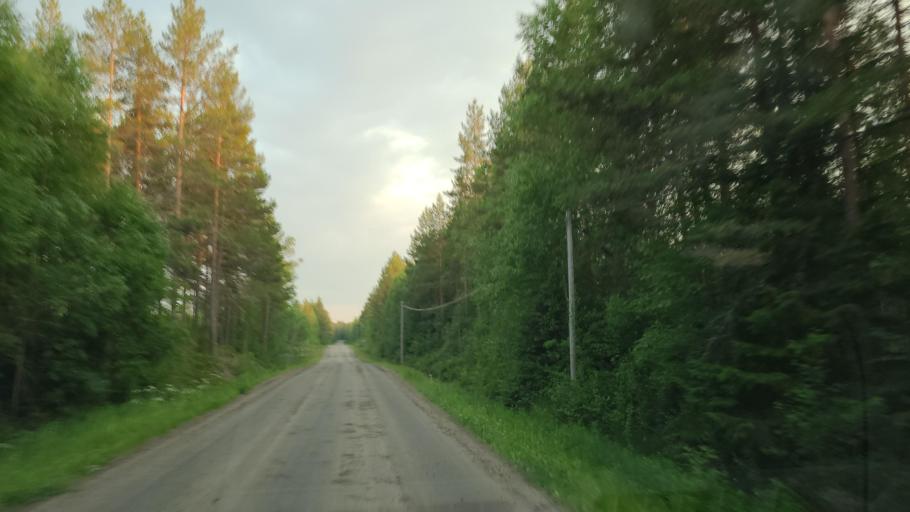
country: SE
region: Vaesterbotten
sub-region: Robertsfors Kommun
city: Robertsfors
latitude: 64.0765
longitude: 20.8863
